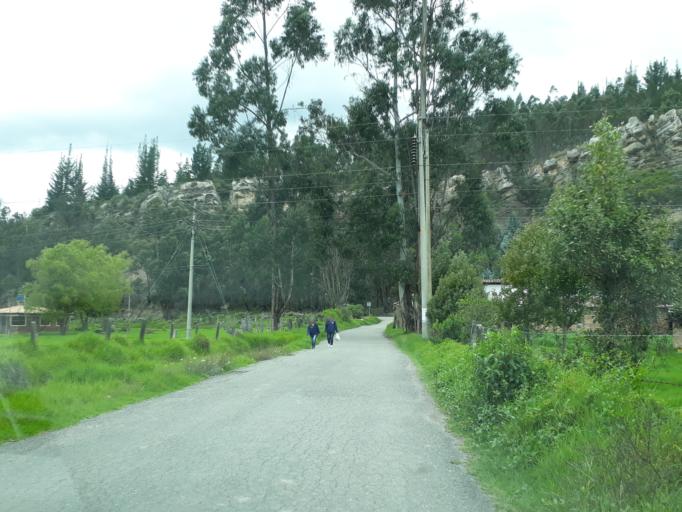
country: CO
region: Cundinamarca
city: Ubate
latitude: 5.2783
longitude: -73.8243
